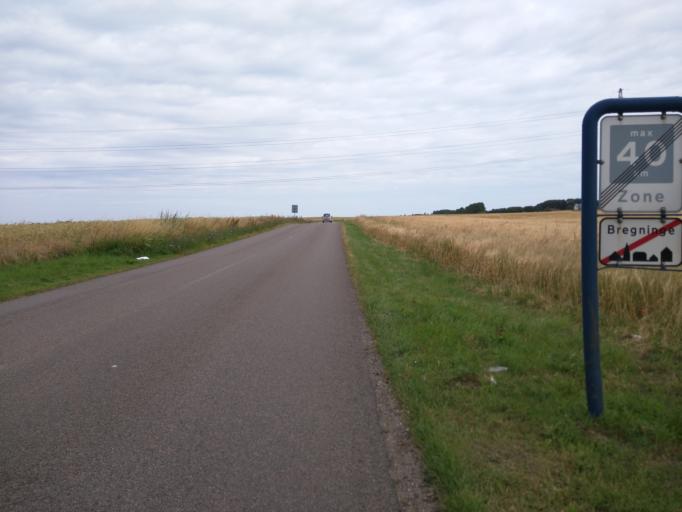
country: DK
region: Zealand
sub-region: Kalundborg Kommune
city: Svebolle
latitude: 55.6885
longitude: 11.3059
